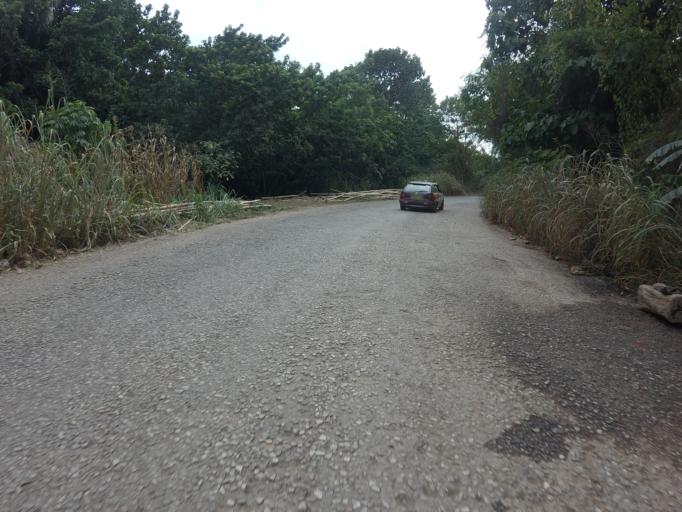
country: GH
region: Volta
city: Ho
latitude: 6.6825
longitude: 0.3434
